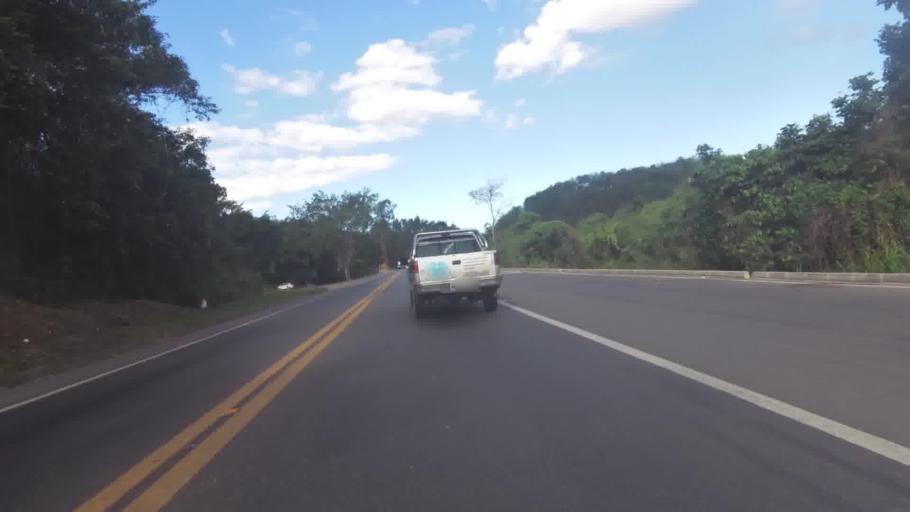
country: BR
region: Espirito Santo
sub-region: Rio Novo Do Sul
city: Rio Novo do Sul
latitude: -20.8660
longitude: -40.9107
